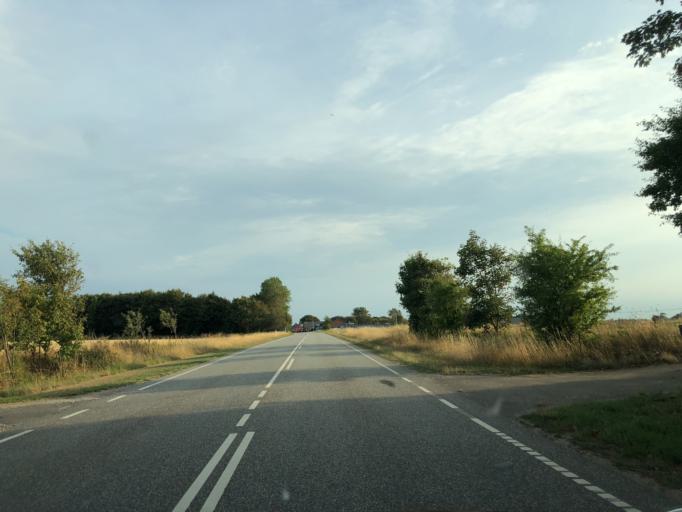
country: DK
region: Central Jutland
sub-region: Struer Kommune
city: Struer
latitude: 56.4759
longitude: 8.5509
